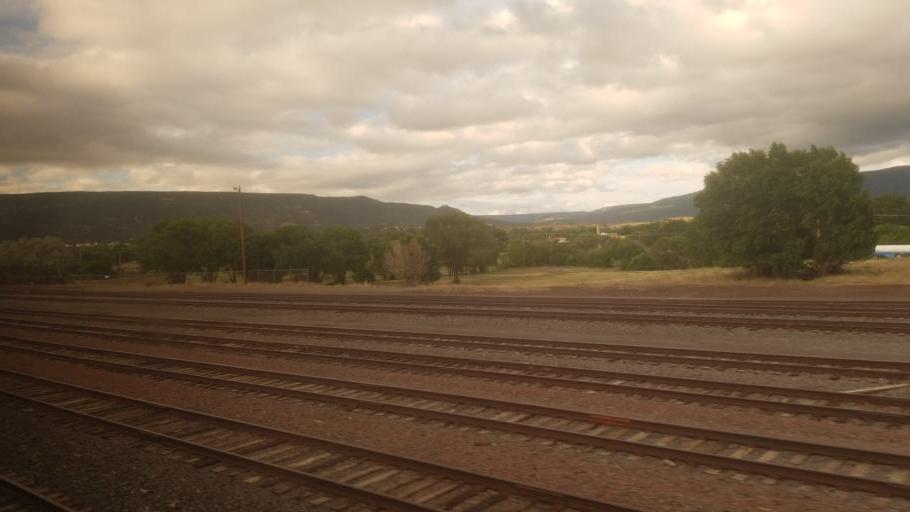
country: US
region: New Mexico
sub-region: Colfax County
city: Raton
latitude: 36.8957
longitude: -104.4386
